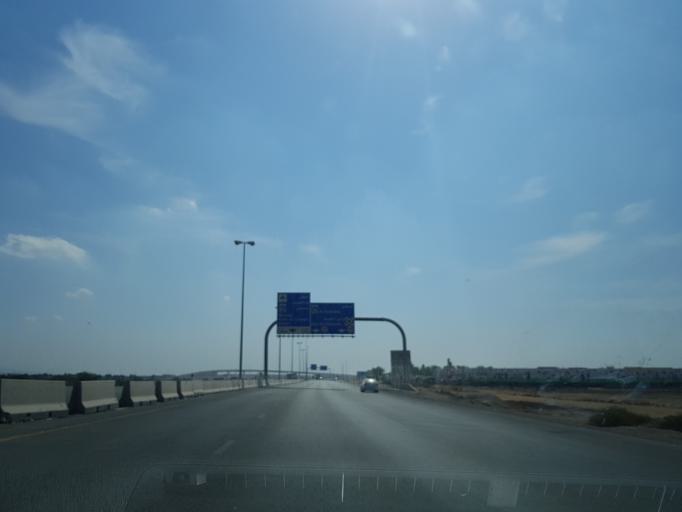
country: AE
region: Ra's al Khaymah
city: Ras al-Khaimah
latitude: 25.8429
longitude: 56.0189
